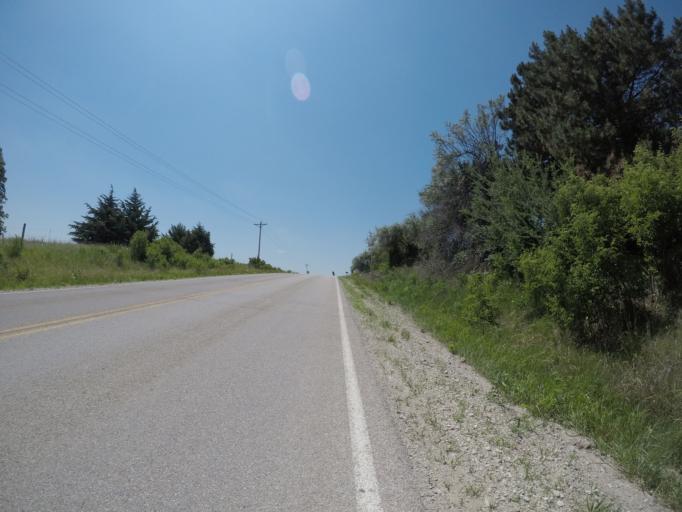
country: US
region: Kansas
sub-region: Pottawatomie County
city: Westmoreland
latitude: 39.2606
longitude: -96.4450
